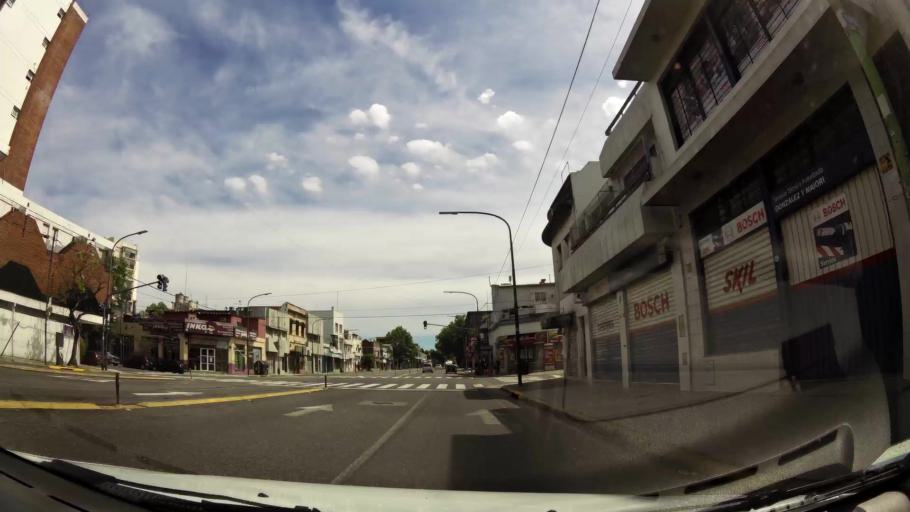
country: AR
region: Buenos Aires F.D.
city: Villa Santa Rita
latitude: -34.6227
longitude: -58.4817
